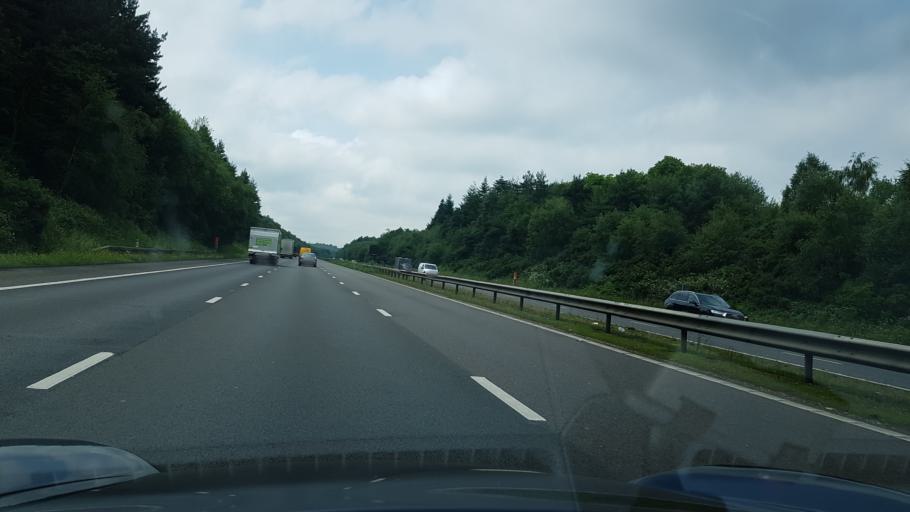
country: GB
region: England
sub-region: West Sussex
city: Maidenbower
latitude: 51.1013
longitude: -0.1483
